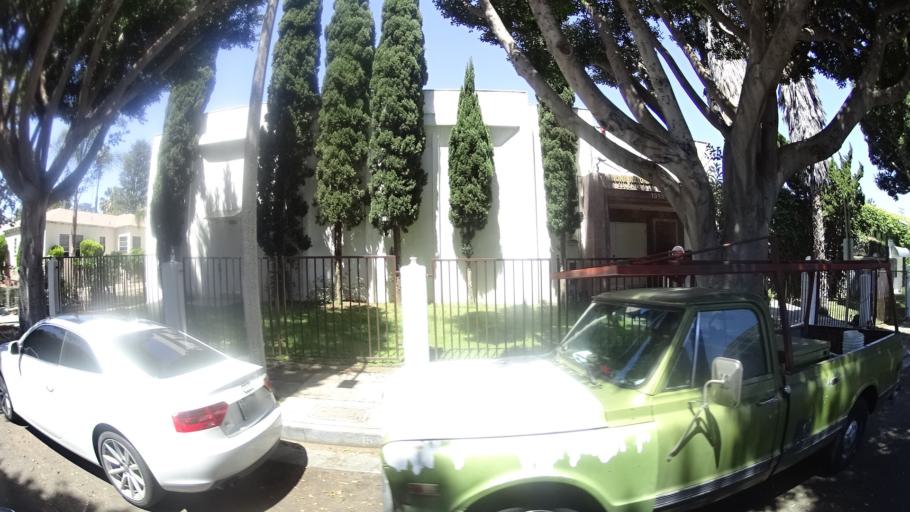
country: US
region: California
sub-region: Los Angeles County
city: Santa Monica
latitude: 34.0361
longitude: -118.4665
